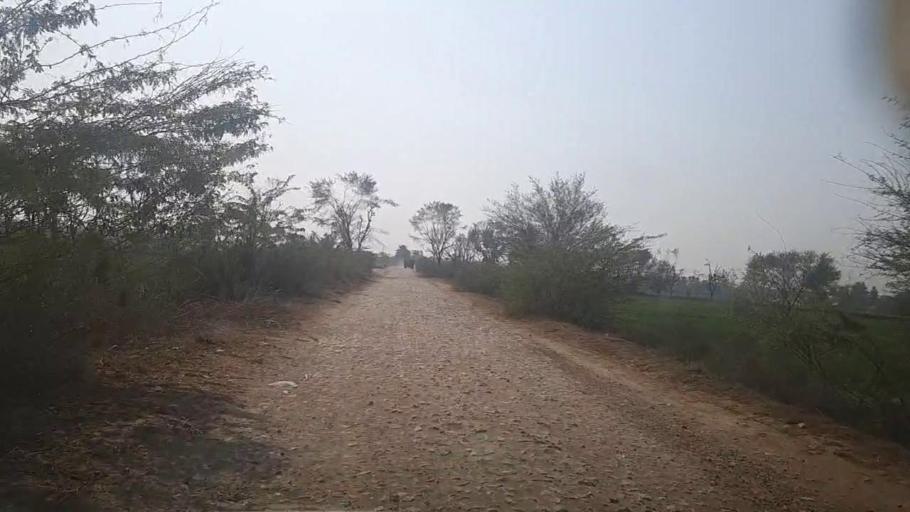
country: PK
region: Sindh
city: Kot Diji
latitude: 27.3645
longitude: 68.7457
